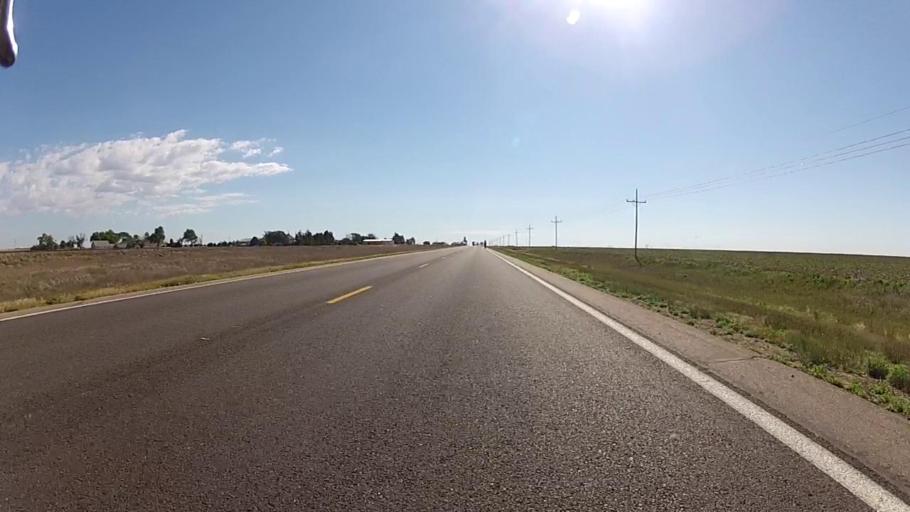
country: US
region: Kansas
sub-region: Gray County
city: Cimarron
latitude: 37.5885
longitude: -100.4813
